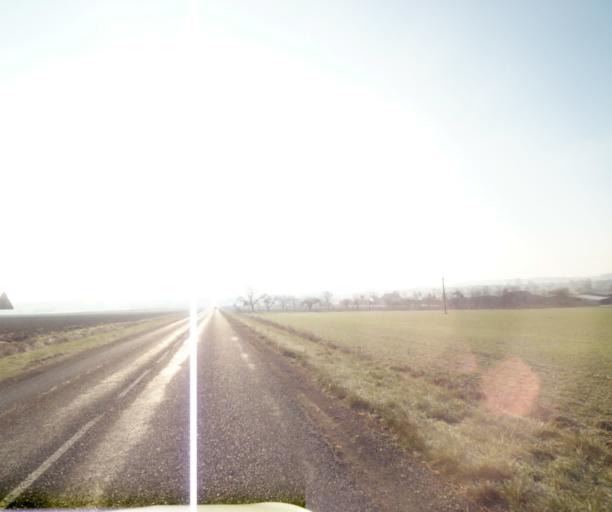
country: FR
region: Champagne-Ardenne
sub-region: Departement de la Haute-Marne
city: Montier-en-Der
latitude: 48.4932
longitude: 4.7555
